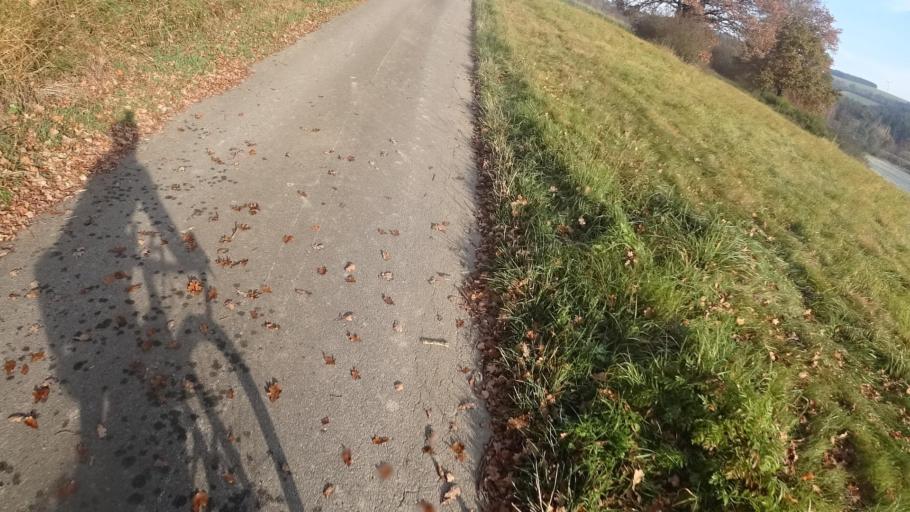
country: DE
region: Rheinland-Pfalz
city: Muhlpfad
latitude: 50.1154
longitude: 7.5601
